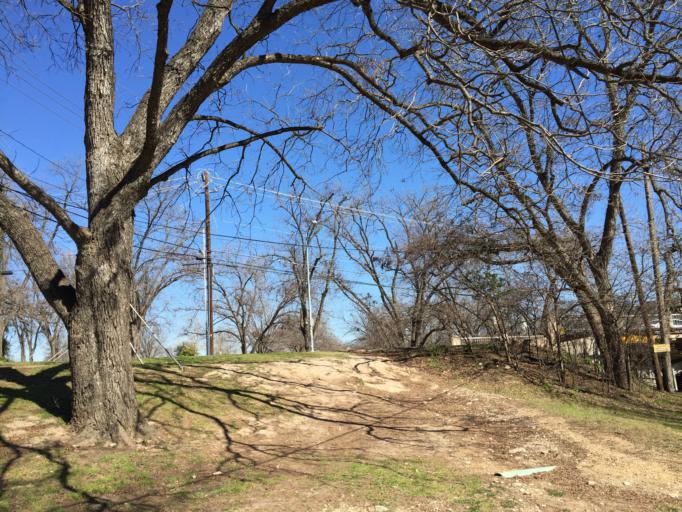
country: US
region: Texas
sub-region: Travis County
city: Austin
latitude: 30.2651
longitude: -97.7660
